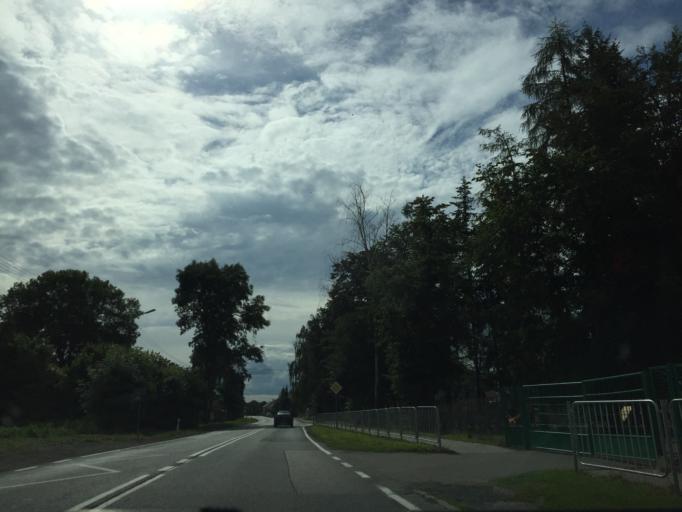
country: PL
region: Lublin Voivodeship
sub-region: Powiat lukowski
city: Trzebieszow
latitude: 51.9898
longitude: 22.5575
